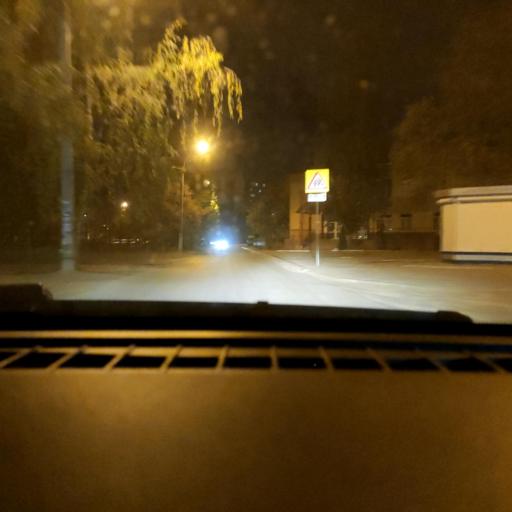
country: RU
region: Voronezj
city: Voronezh
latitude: 51.6424
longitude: 39.2699
